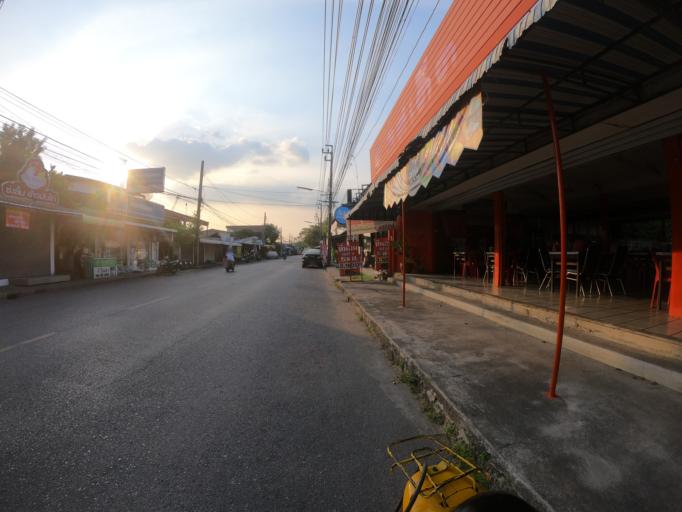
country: TH
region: Bangkok
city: Lat Phrao
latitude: 13.8313
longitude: 100.6063
